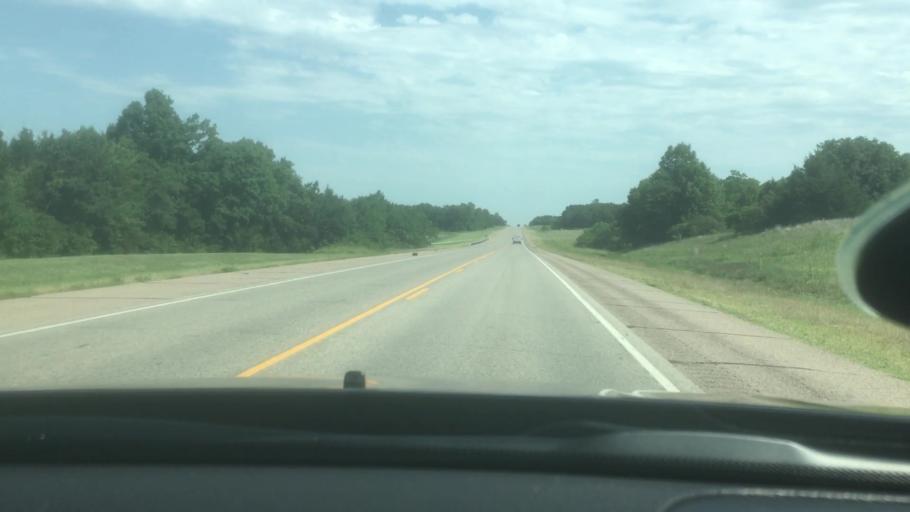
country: US
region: Oklahoma
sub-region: Seminole County
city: Konawa
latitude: 35.0016
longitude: -96.9314
